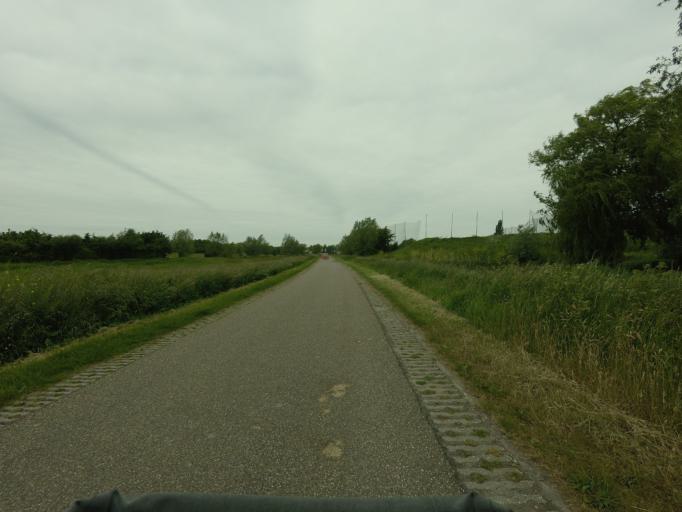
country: NL
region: North Holland
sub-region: Gemeente Medemblik
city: Medemblik
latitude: 52.7451
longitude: 5.1124
